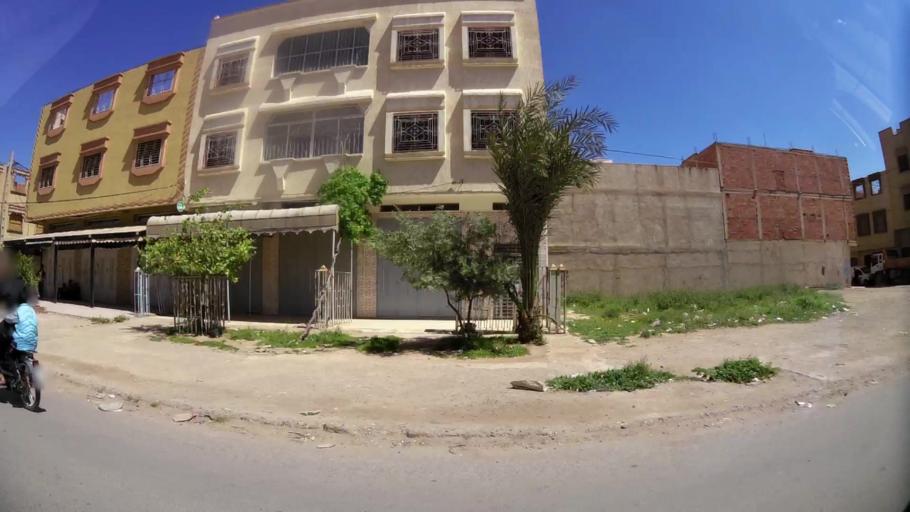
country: MA
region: Oriental
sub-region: Oujda-Angad
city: Oujda
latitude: 34.6900
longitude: -1.9409
